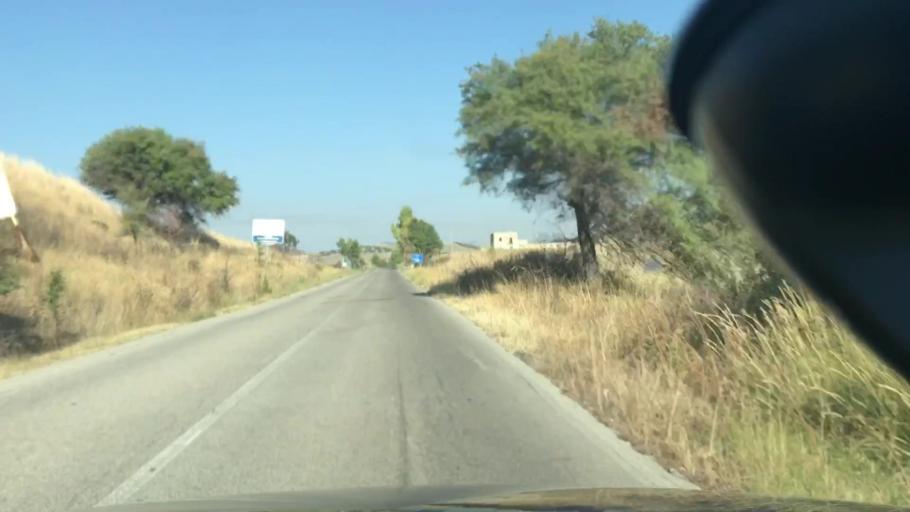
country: IT
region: Basilicate
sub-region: Provincia di Matera
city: La Martella
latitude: 40.6667
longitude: 16.4895
